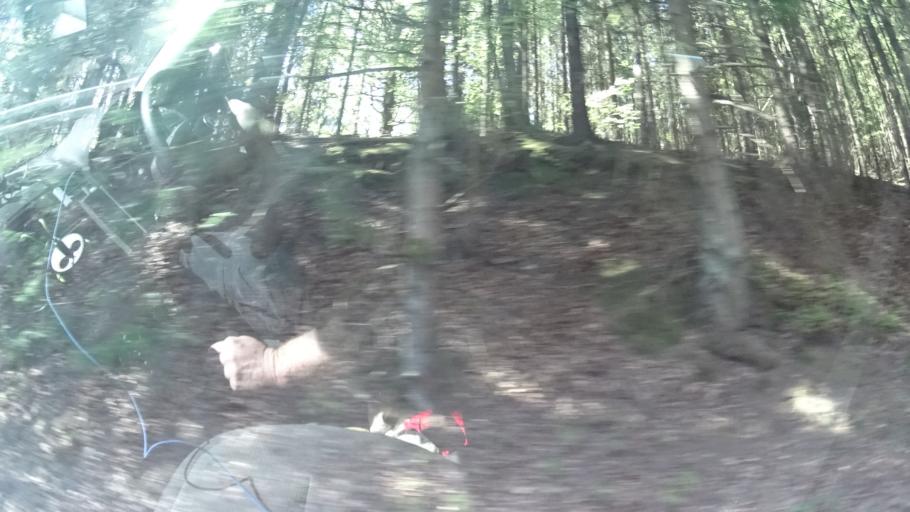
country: DE
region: Thuringia
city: Frauenwald
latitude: 50.5145
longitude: 10.8357
